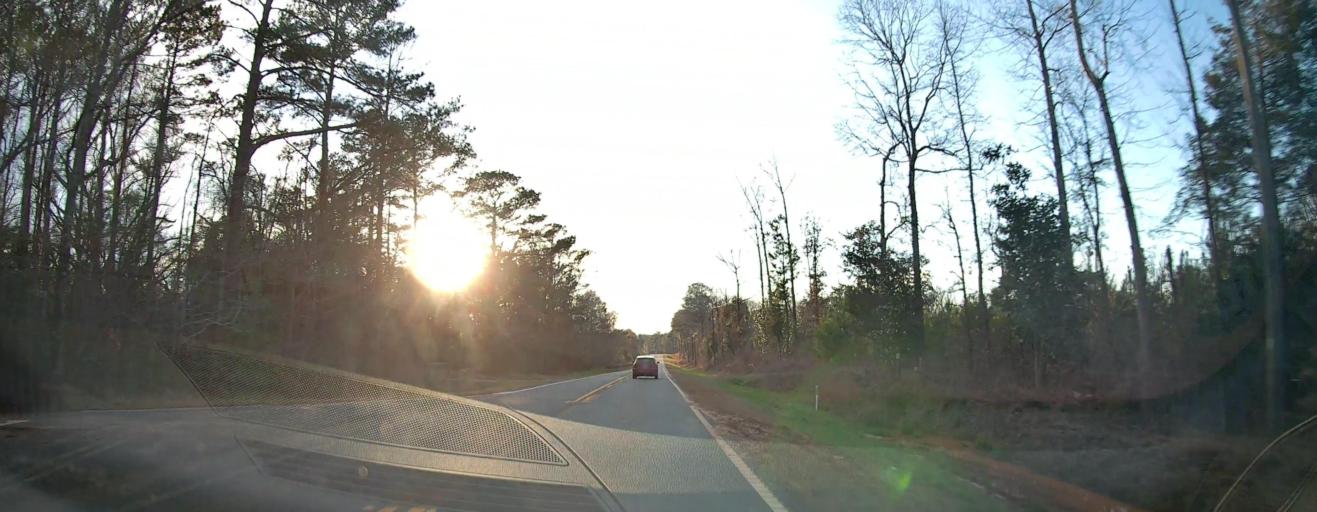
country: US
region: Georgia
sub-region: Talbot County
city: Sardis
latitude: 32.7200
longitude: -84.6626
